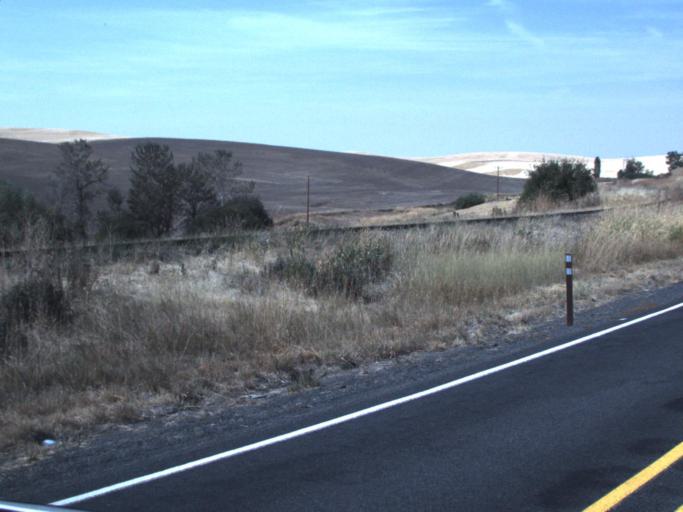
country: US
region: Washington
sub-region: Whitman County
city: Pullman
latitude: 46.9668
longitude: -117.1105
